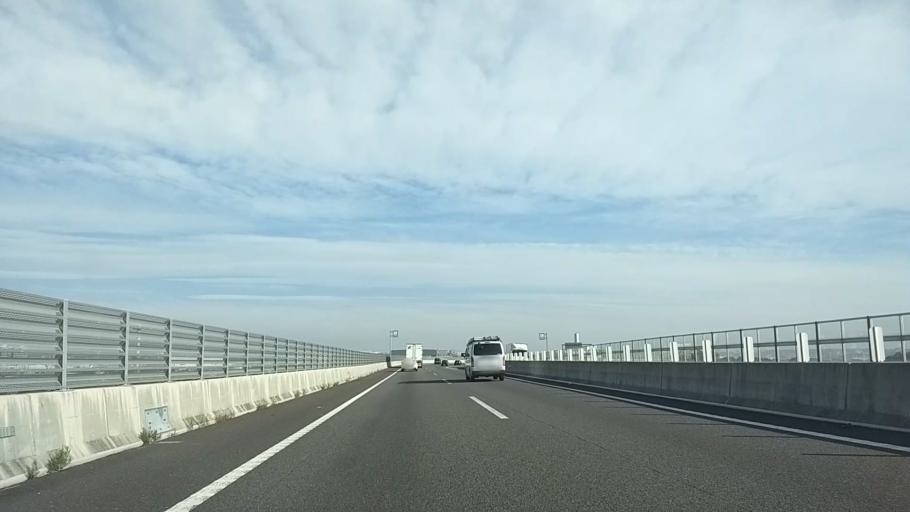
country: JP
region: Kanagawa
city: Atsugi
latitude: 35.4464
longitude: 139.3741
